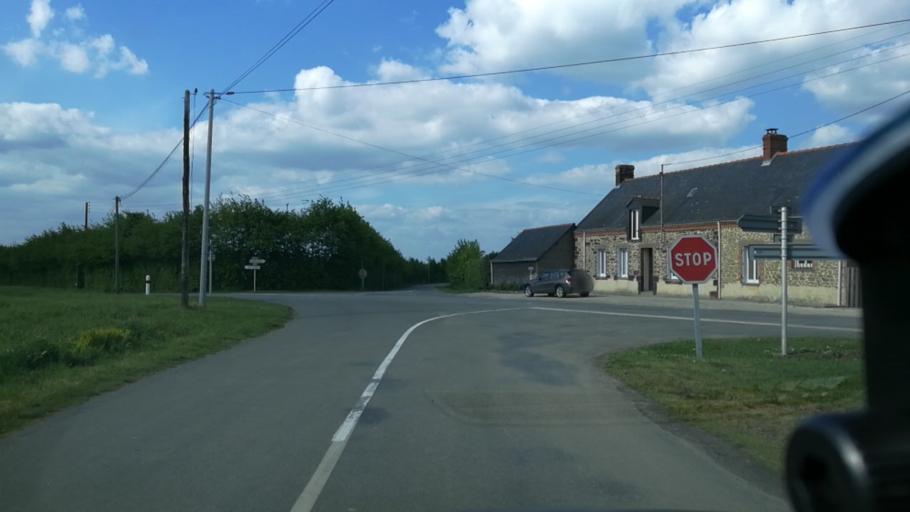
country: FR
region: Brittany
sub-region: Departement d'Ille-et-Vilaine
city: Martigne-Ferchaud
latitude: 47.8821
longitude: -1.3211
